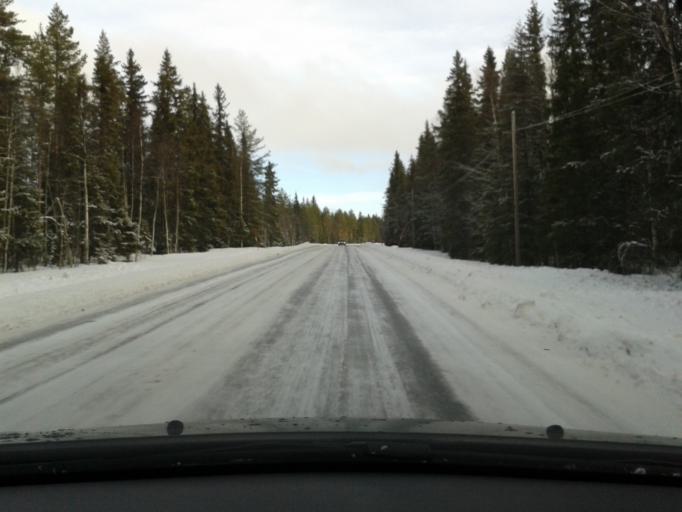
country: SE
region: Vaesterbotten
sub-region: Vilhelmina Kommun
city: Vilhelmina
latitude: 64.6370
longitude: 16.4481
